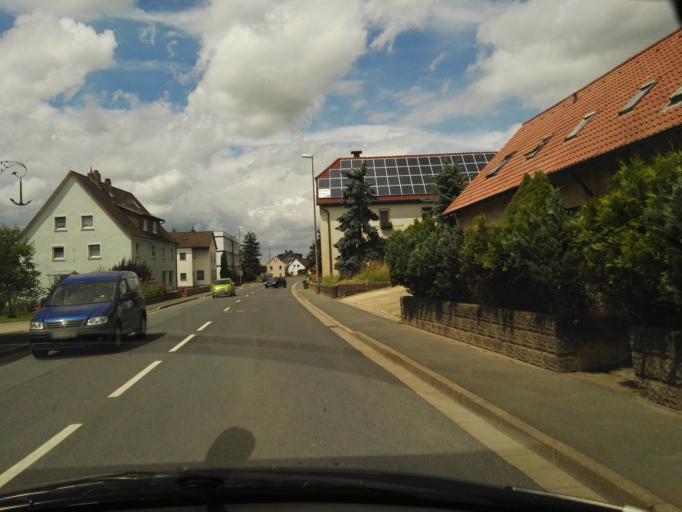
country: DE
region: Bavaria
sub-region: Upper Franconia
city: Burgkunstadt
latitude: 50.1455
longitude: 11.2294
